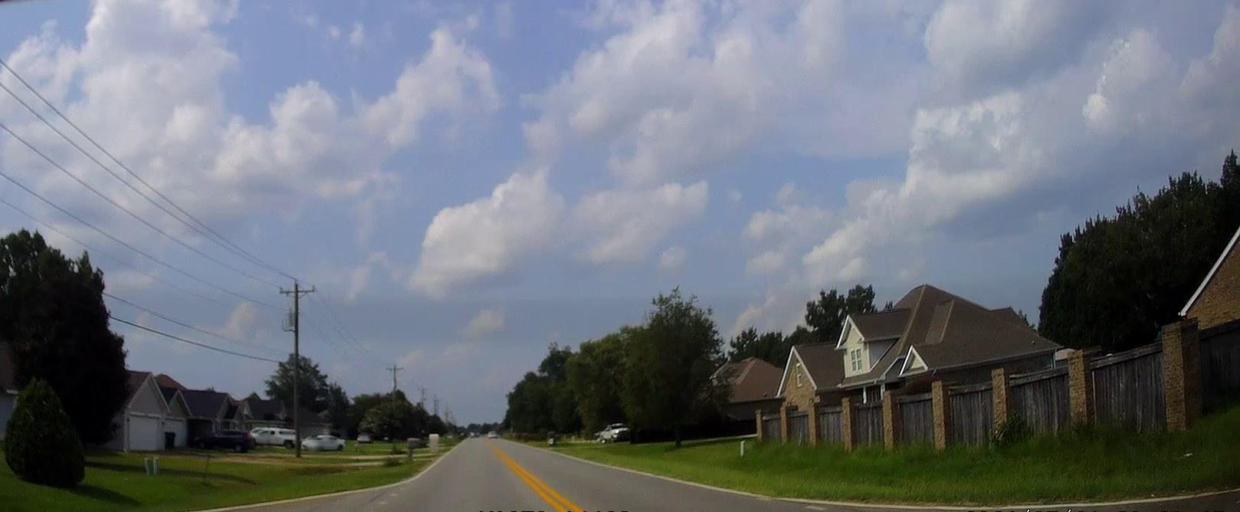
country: US
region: Georgia
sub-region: Houston County
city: Centerville
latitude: 32.5597
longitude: -83.6522
